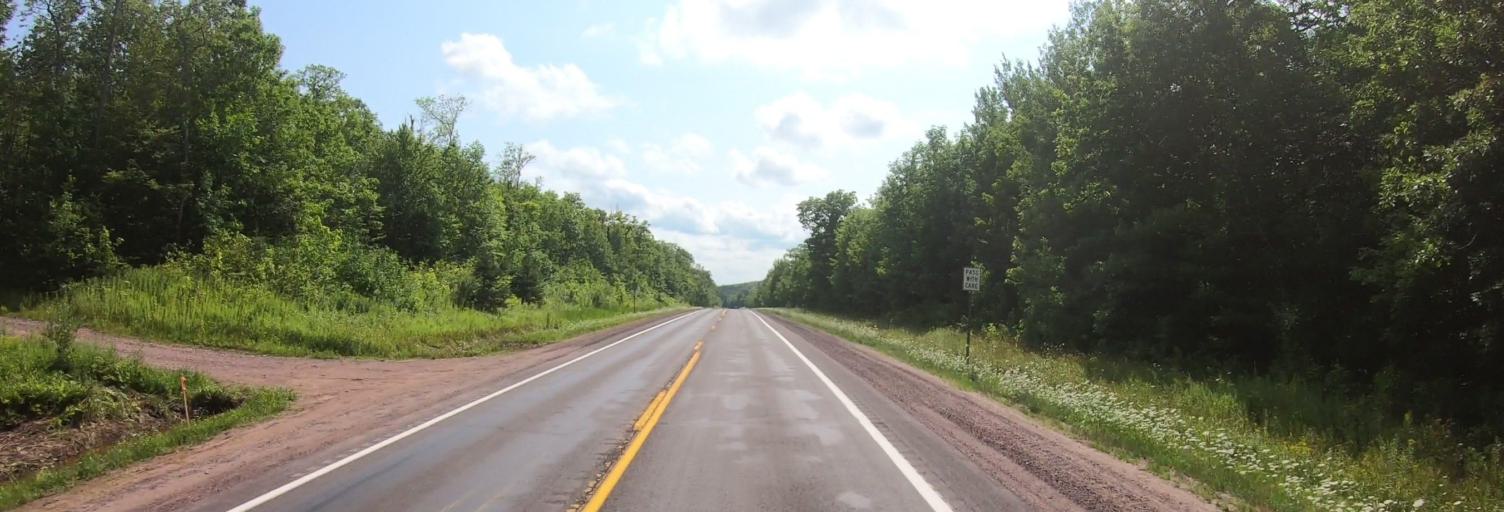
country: US
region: Michigan
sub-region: Ontonagon County
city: Ontonagon
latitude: 46.8445
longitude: -88.9844
